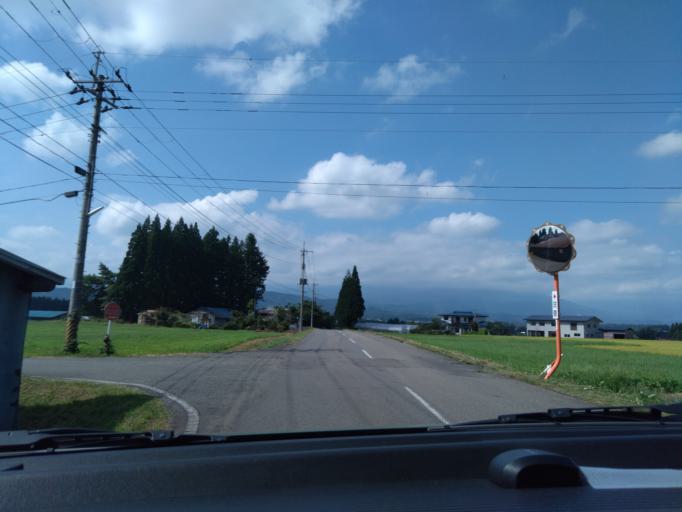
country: JP
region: Iwate
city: Shizukuishi
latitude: 39.6779
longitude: 140.9608
